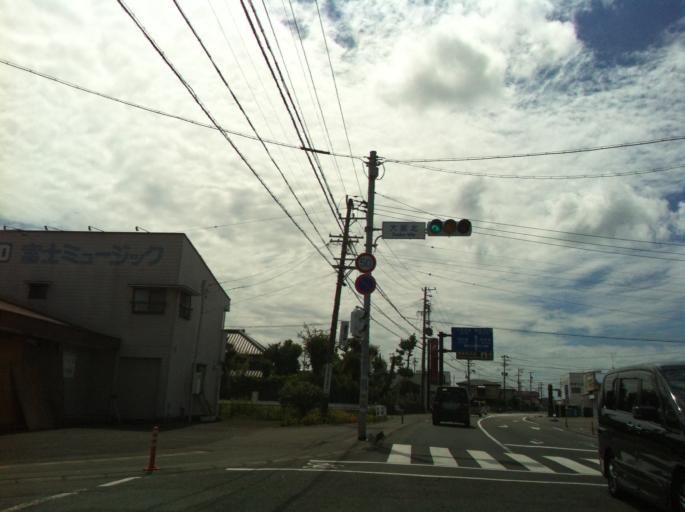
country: JP
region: Shizuoka
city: Kakegawa
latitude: 34.6699
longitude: 138.0455
